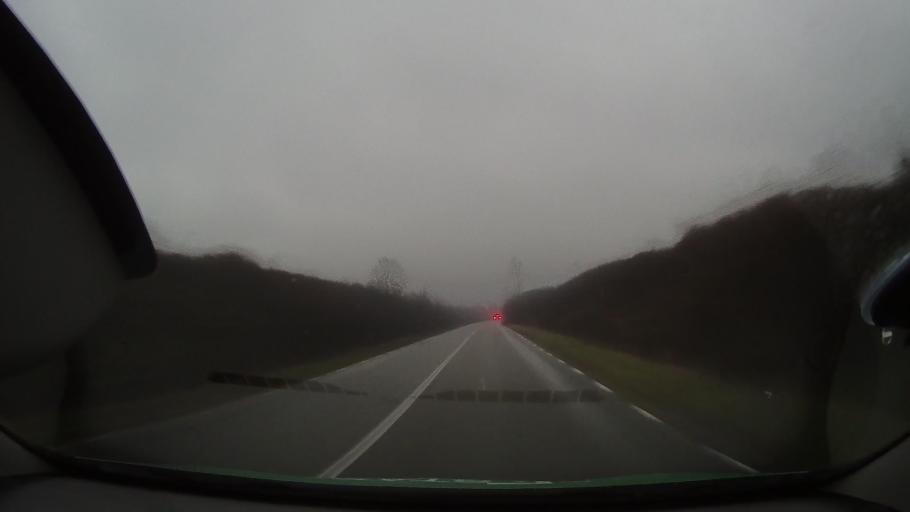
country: RO
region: Arad
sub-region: Comuna Craiova
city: Craiova
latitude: 46.5997
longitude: 21.9707
